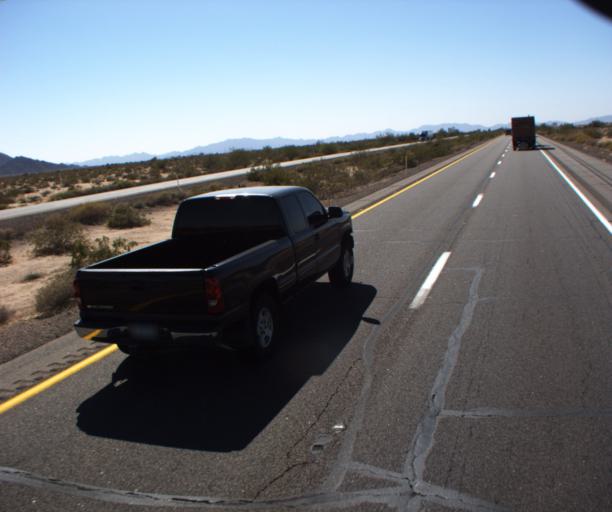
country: US
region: Arizona
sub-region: Yuma County
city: Wellton
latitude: 32.6912
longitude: -113.9696
